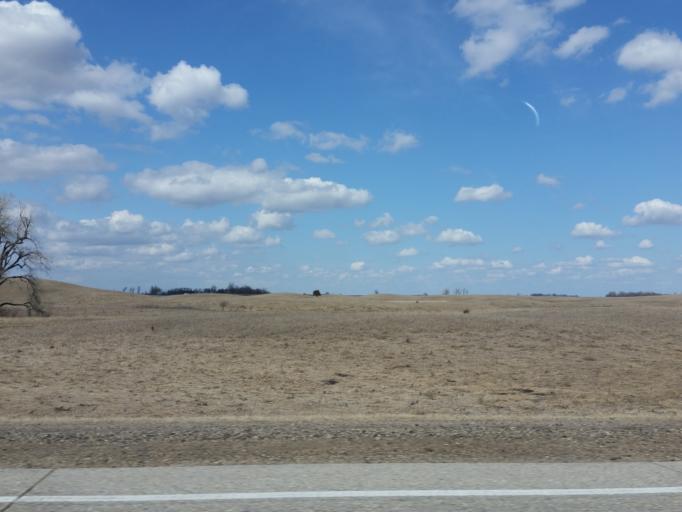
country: US
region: South Dakota
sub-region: Deuel County
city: Clear Lake
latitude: 44.8901
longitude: -96.7188
